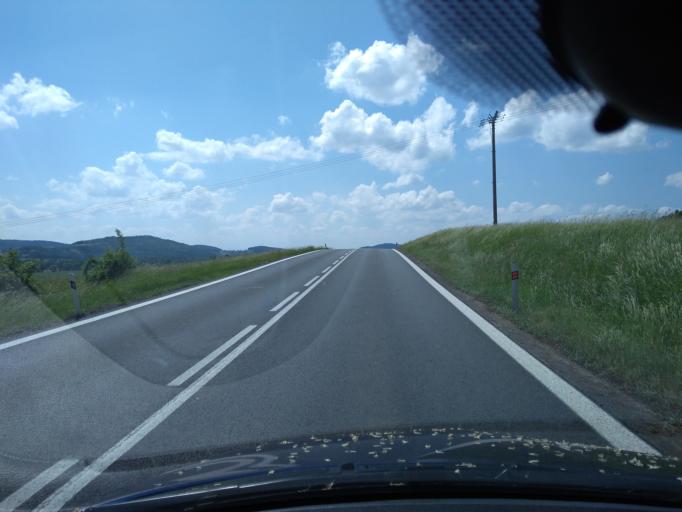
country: CZ
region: Plzensky
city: Prestice
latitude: 49.5650
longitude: 13.3242
